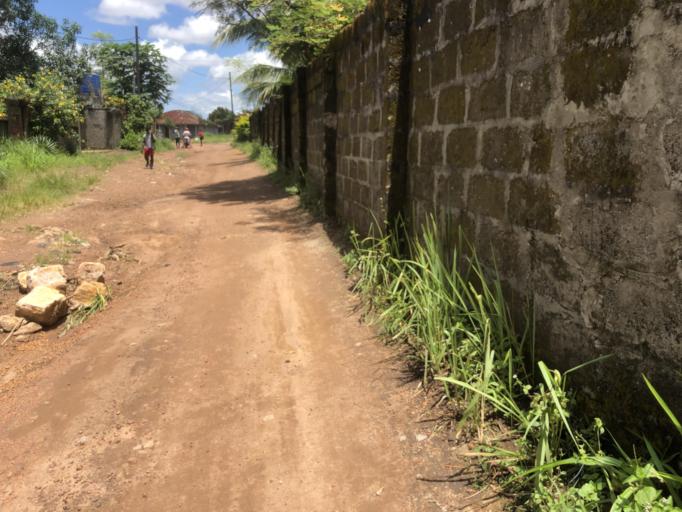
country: SL
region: Northern Province
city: Makeni
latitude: 8.8576
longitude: -12.0457
